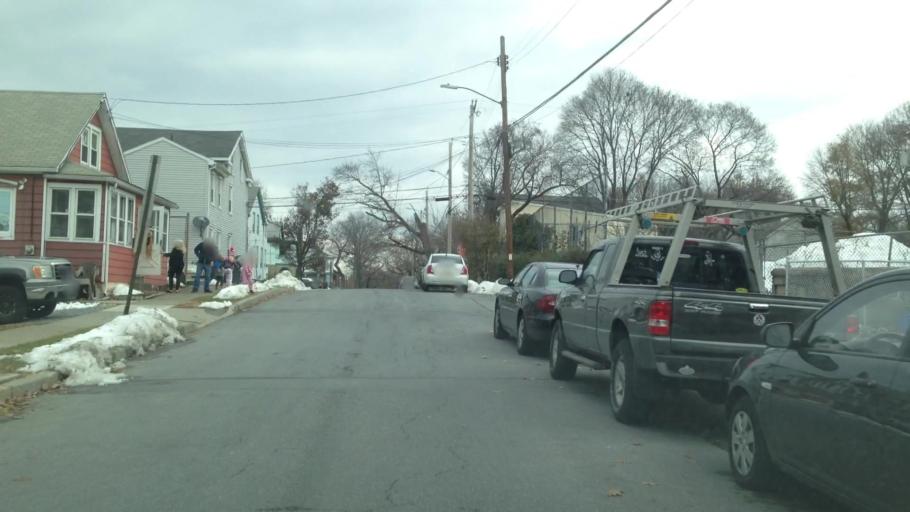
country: US
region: New York
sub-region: Dutchess County
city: Poughkeepsie
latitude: 41.7115
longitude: -73.9361
